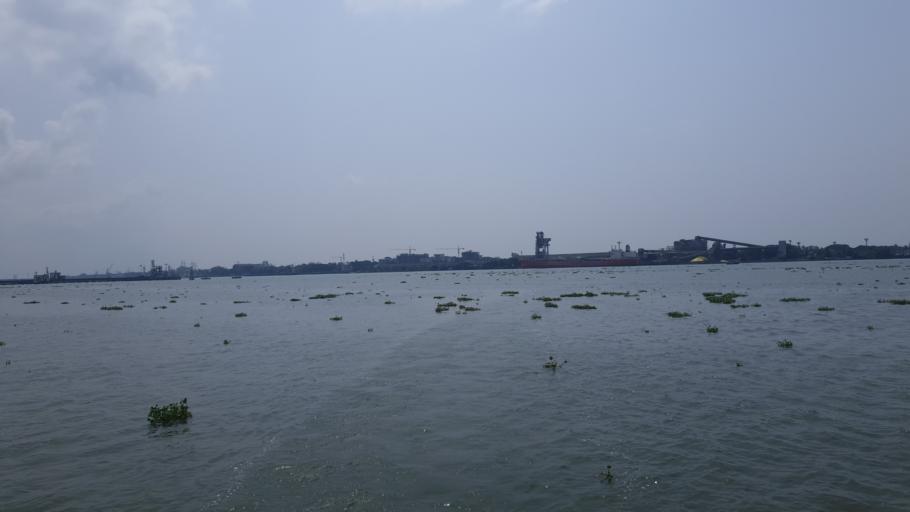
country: IN
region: Kerala
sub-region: Ernakulam
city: Cochin
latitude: 9.9725
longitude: 76.2769
